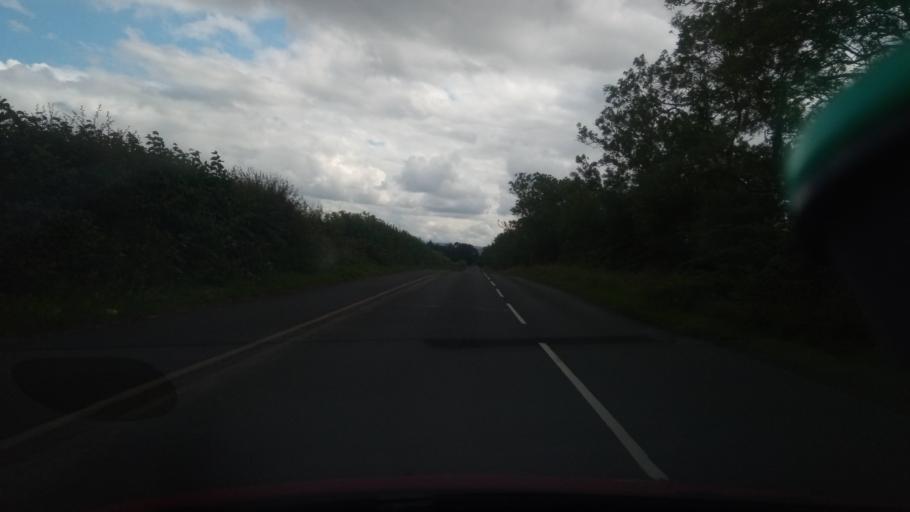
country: GB
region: Scotland
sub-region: East Lothian
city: Ormiston
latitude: 55.9252
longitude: -2.9371
